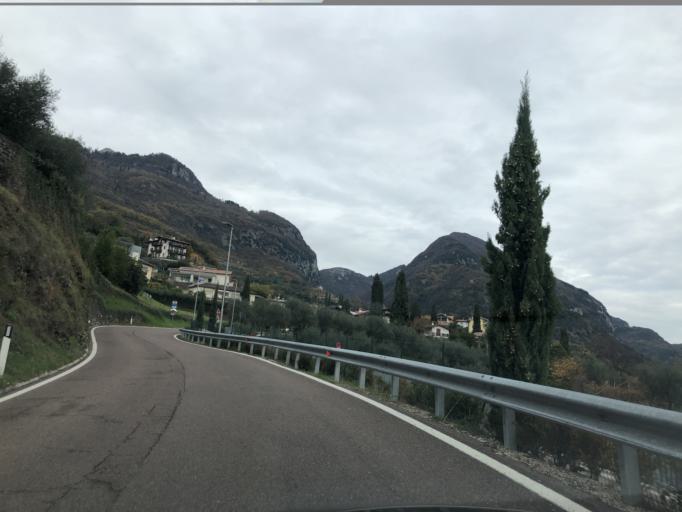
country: IT
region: Trentino-Alto Adige
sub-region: Provincia di Trento
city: Tenno
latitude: 45.9159
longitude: 10.8473
